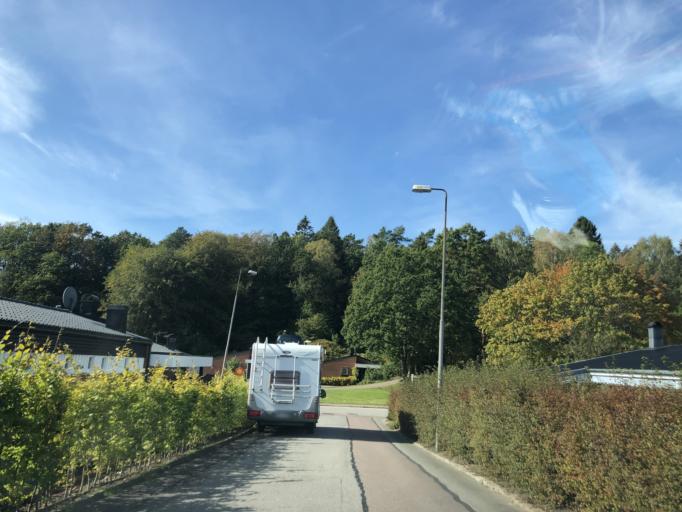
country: SE
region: Vaestra Goetaland
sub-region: Molndal
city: Moelndal
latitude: 57.6660
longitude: 12.0471
